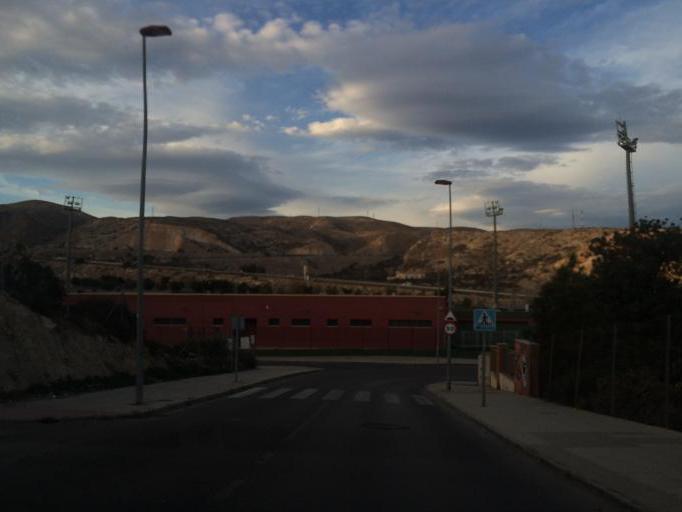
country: ES
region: Andalusia
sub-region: Provincia de Almeria
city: Almeria
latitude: 36.8510
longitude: -2.4702
